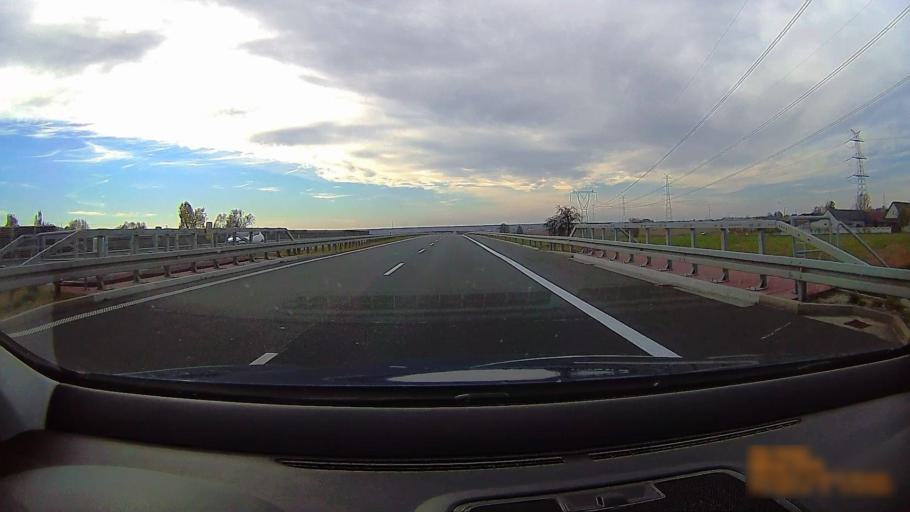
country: PL
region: Greater Poland Voivodeship
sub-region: Powiat ostrowski
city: Przygodzice
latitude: 51.6055
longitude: 17.8544
